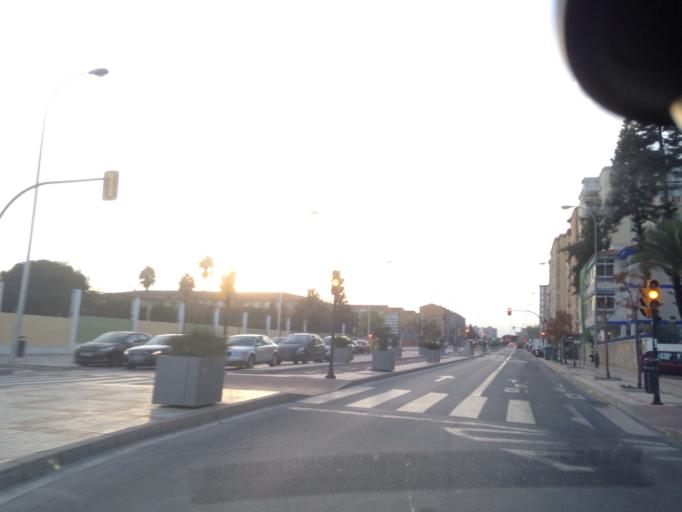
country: ES
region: Andalusia
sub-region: Provincia de Malaga
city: Malaga
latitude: 36.7192
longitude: -4.4494
